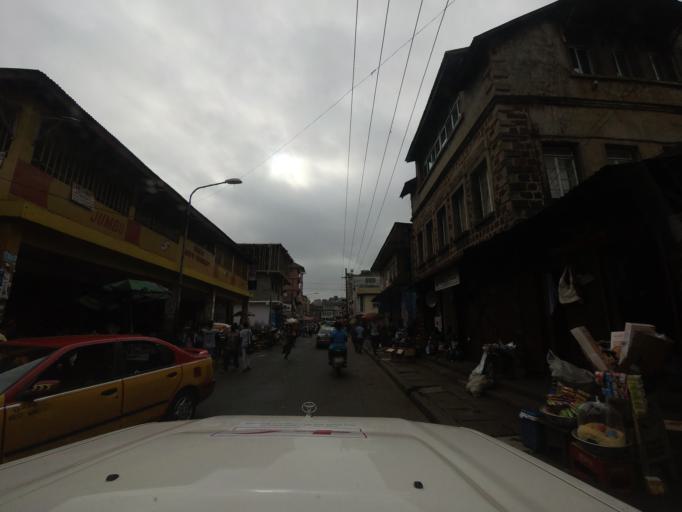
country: SL
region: Western Area
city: Freetown
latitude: 8.4834
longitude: -13.2405
